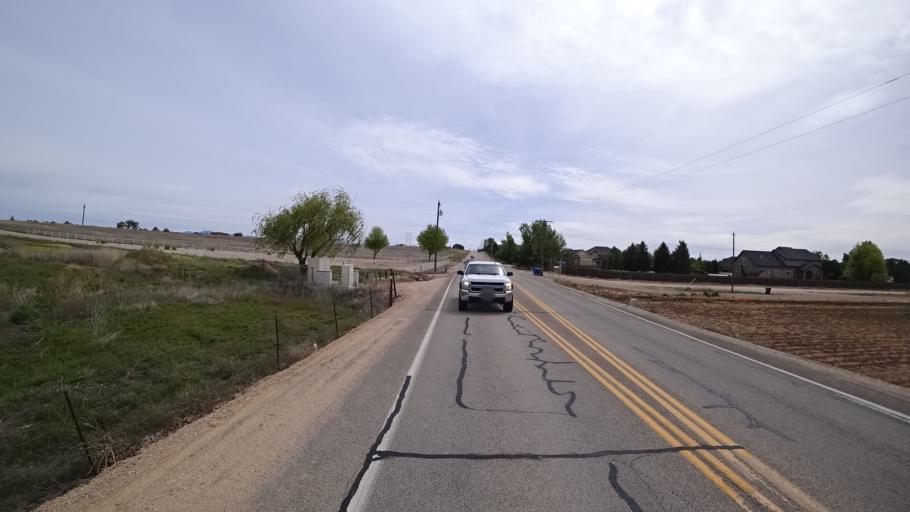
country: US
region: Idaho
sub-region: Ada County
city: Meridian
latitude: 43.5612
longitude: -116.4442
